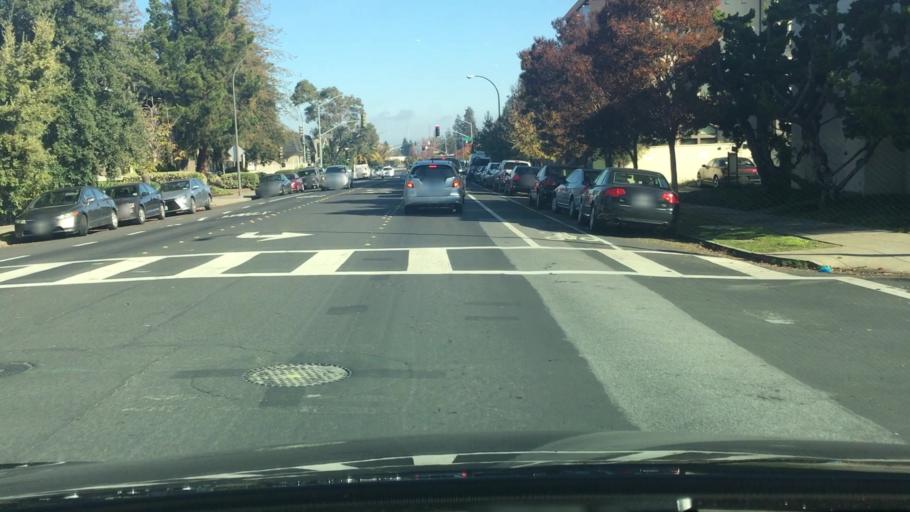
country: US
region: California
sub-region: San Mateo County
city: Redwood City
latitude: 37.4896
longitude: -122.2327
